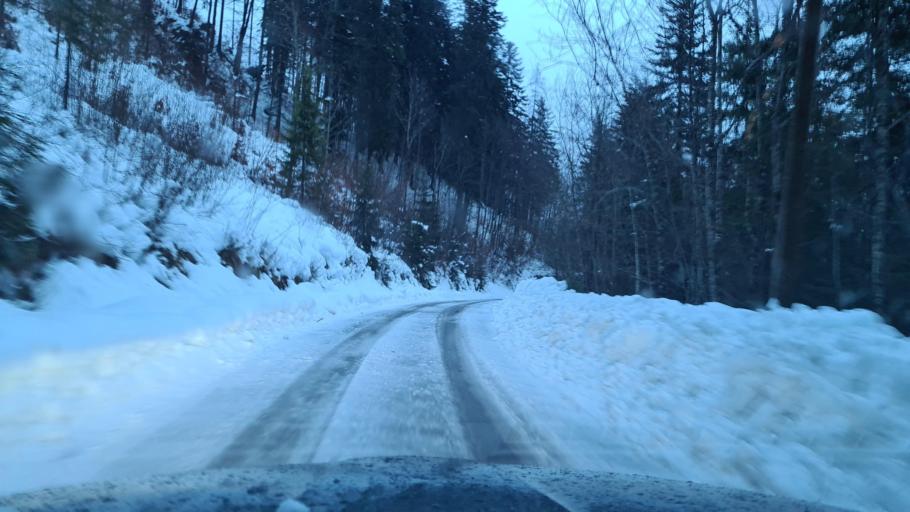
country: AT
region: Salzburg
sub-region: Politischer Bezirk Sankt Johann im Pongau
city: Werfen
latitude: 47.4867
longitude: 13.1568
